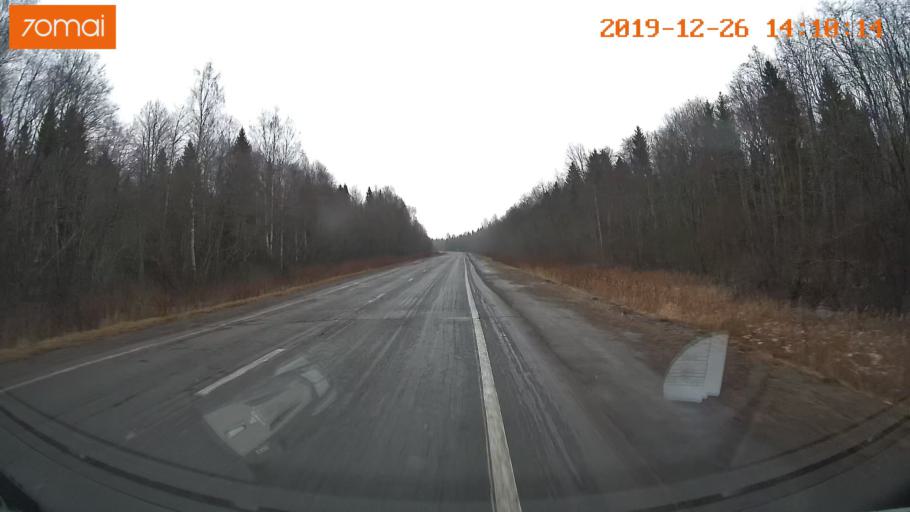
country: RU
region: Jaroslavl
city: Poshekhon'ye
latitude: 58.5084
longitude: 38.9494
